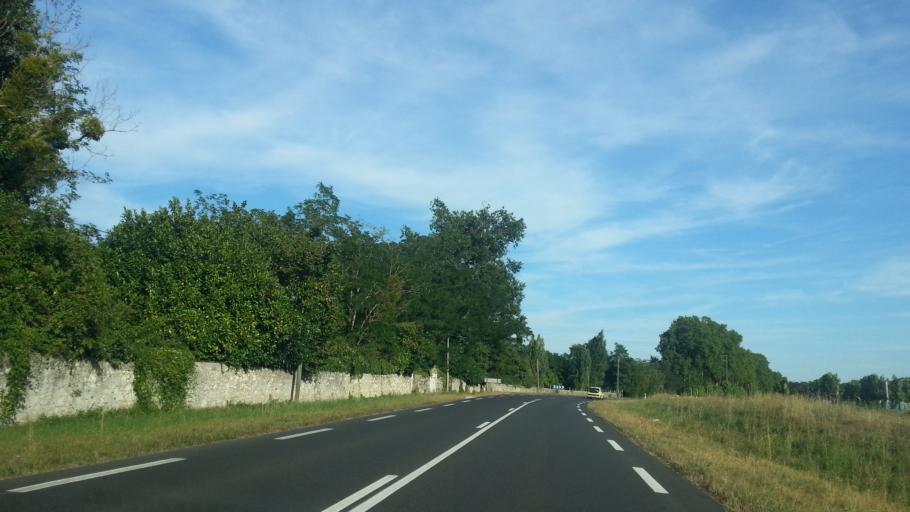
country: FR
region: Aquitaine
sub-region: Departement de la Gironde
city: Paillet
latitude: 44.6703
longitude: -0.3919
